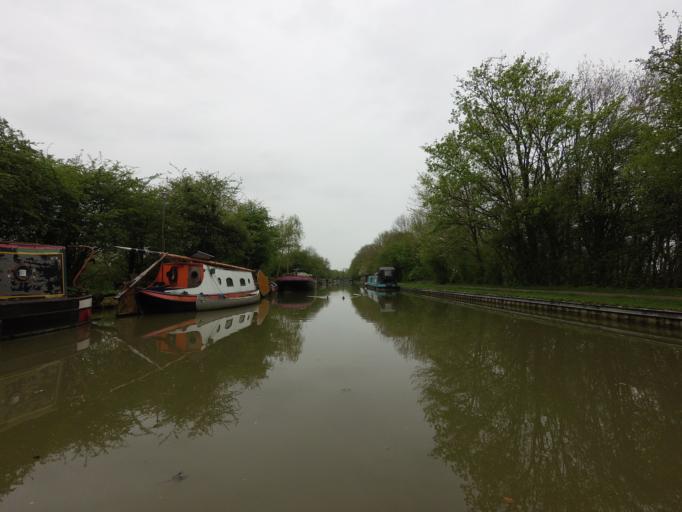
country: GB
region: England
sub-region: Milton Keynes
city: Stony Stratford
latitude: 52.0702
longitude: -0.8364
